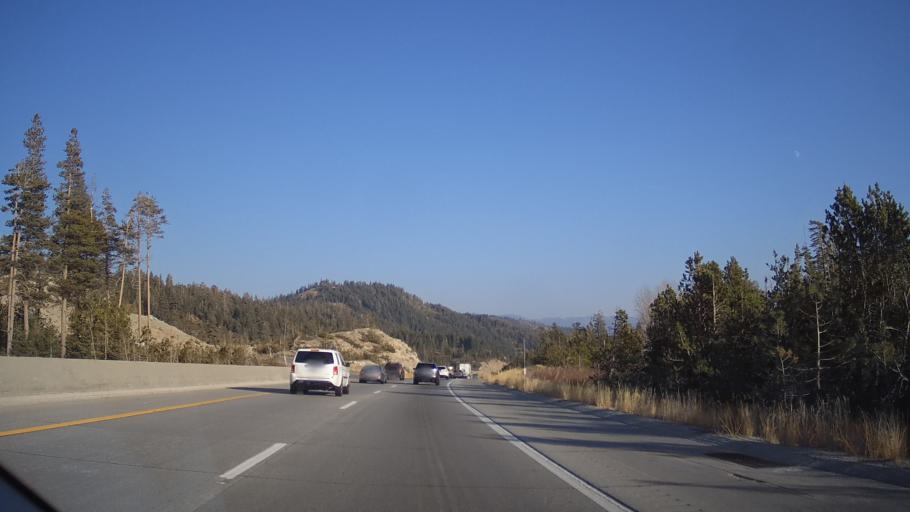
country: US
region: California
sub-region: Nevada County
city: Truckee
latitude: 39.3428
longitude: -120.3338
